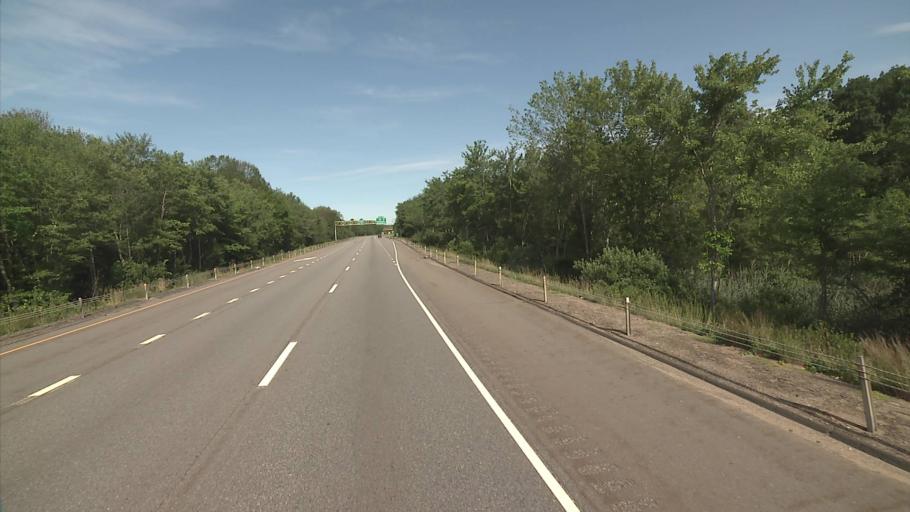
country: US
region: Connecticut
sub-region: New London County
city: Colchester
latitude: 41.5674
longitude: -72.3318
